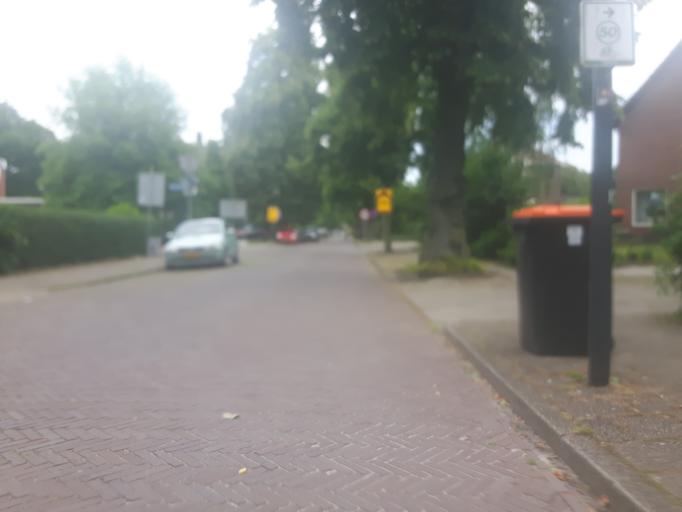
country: NL
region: Overijssel
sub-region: Gemeente Hengelo
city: Hengelo
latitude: 52.2611
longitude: 6.8053
